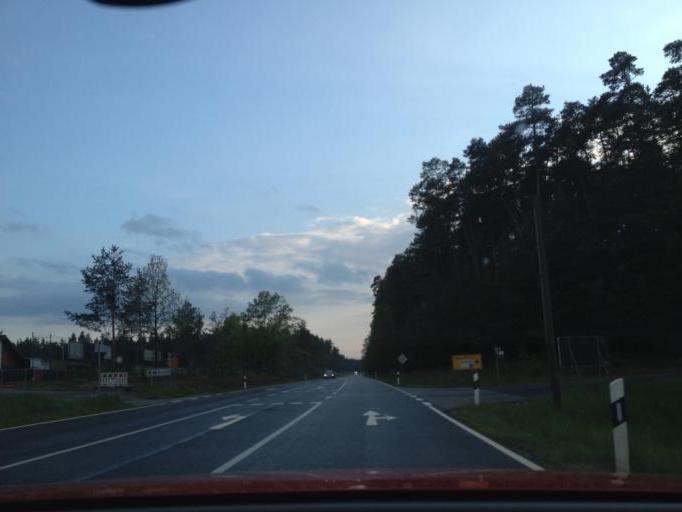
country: DE
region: Bavaria
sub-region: Upper Palatinate
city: Etzenricht
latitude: 49.6171
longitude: 12.0861
